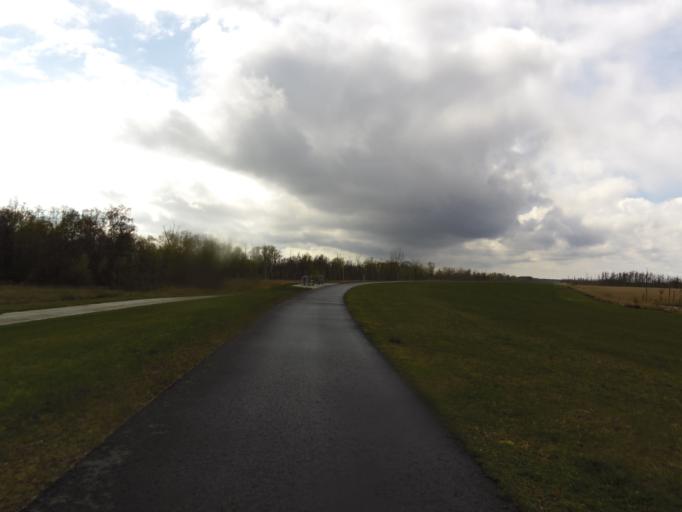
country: DE
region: Mecklenburg-Vorpommern
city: Altenpleen
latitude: 54.4316
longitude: 12.8512
